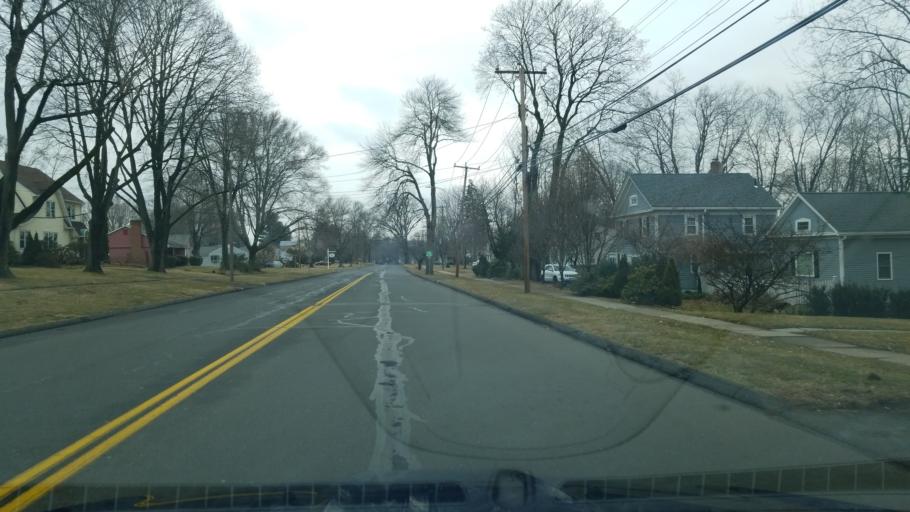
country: US
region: Connecticut
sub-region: Hartford County
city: Wethersfield
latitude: 41.6891
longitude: -72.6714
